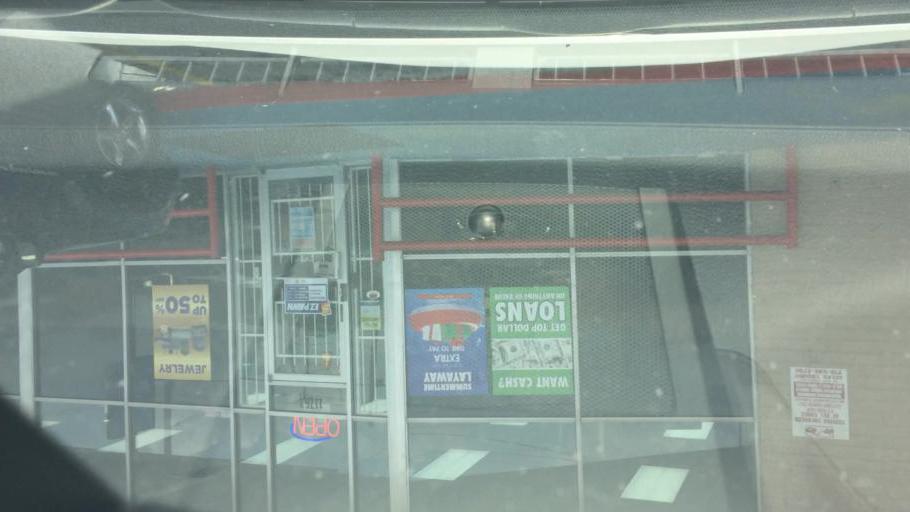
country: US
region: Texas
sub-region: Bexar County
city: Castle Hills
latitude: 29.5481
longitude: -98.5104
